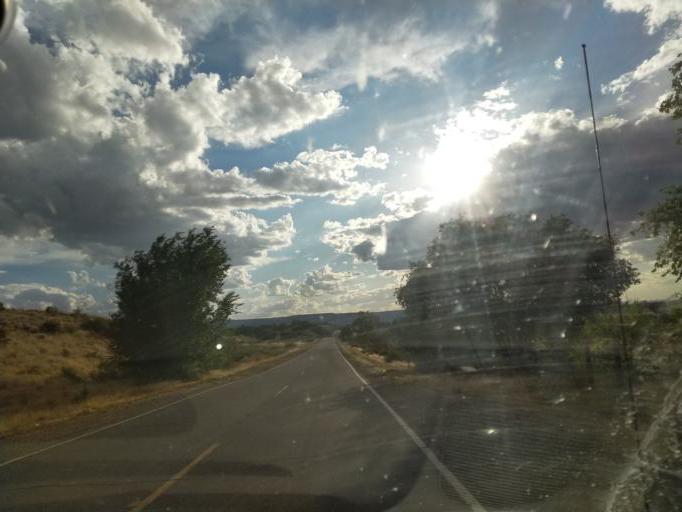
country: US
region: Colorado
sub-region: Mesa County
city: Clifton
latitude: 39.0554
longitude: -108.4534
